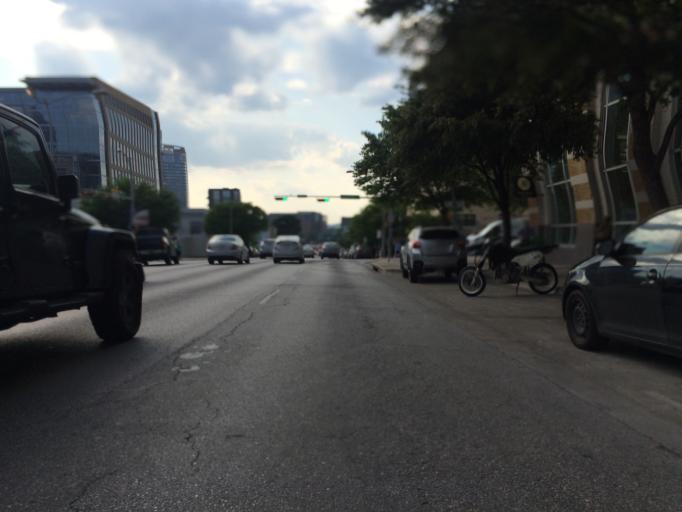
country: US
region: Texas
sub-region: Travis County
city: Austin
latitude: 30.2689
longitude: -97.7457
